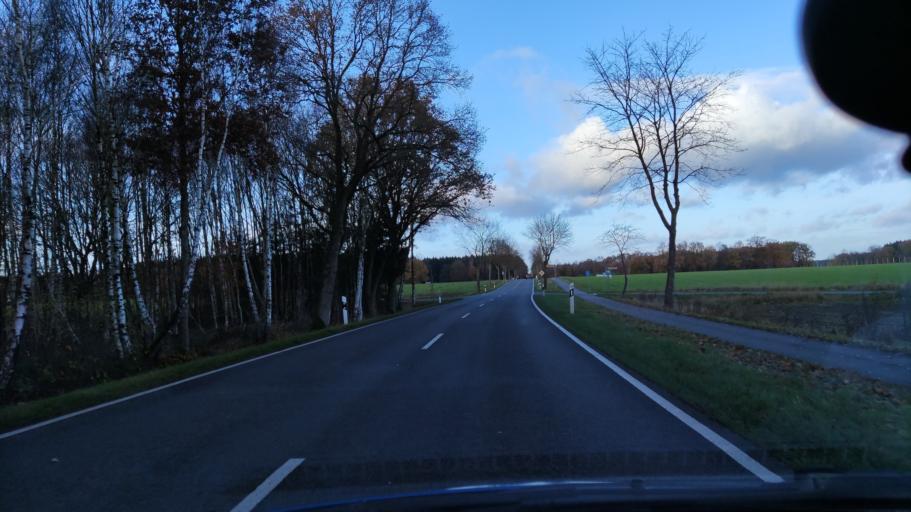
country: DE
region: Lower Saxony
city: Schneverdingen
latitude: 53.0550
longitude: 9.8201
